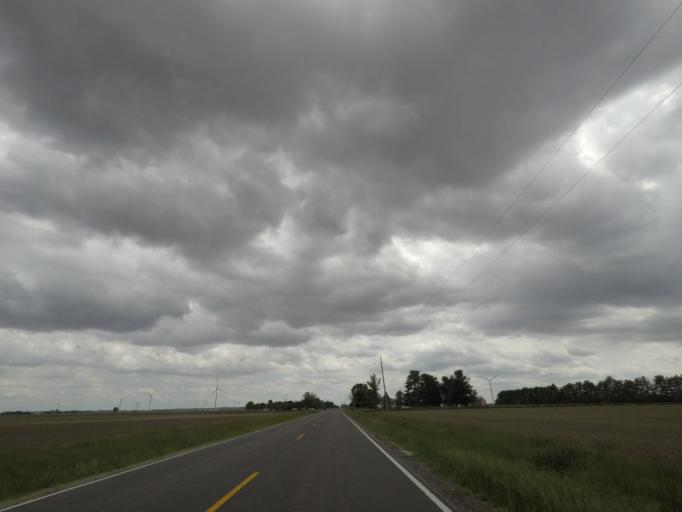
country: US
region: Illinois
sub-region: Macon County
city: Warrensburg
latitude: 39.9962
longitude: -89.0857
